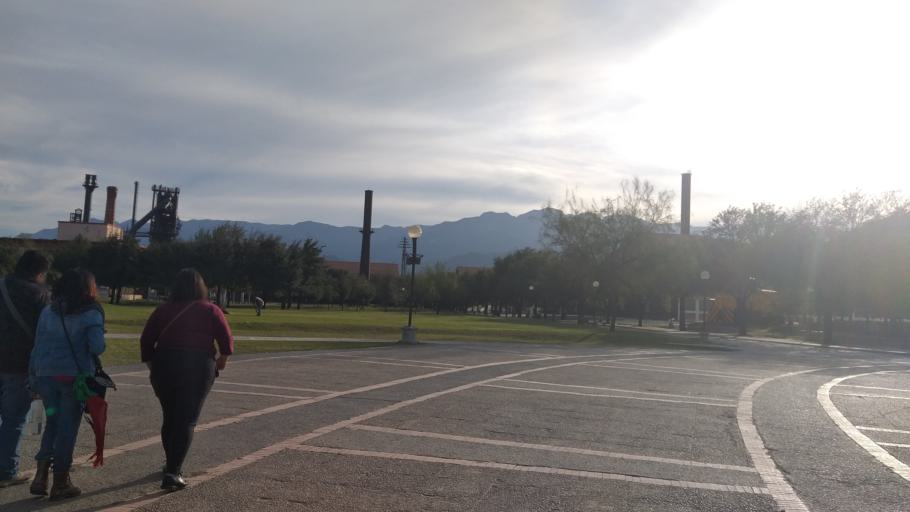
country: MX
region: Nuevo Leon
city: Guadalupe
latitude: 25.6804
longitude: -100.2827
